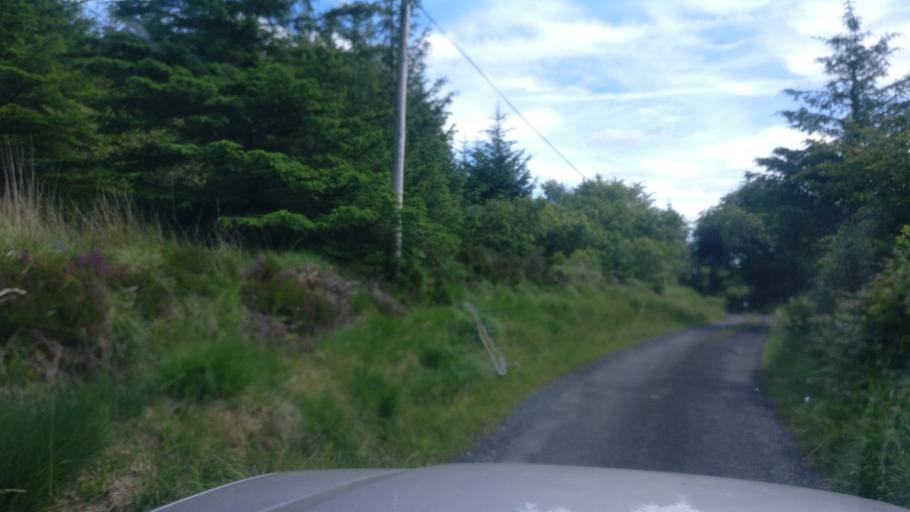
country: IE
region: Connaught
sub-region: County Galway
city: Gort
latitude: 53.0768
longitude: -8.7094
